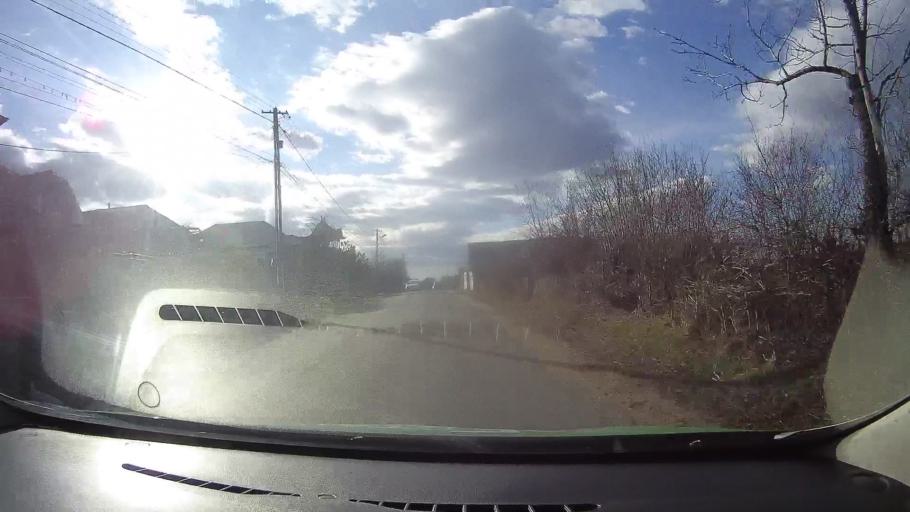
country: RO
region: Dambovita
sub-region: Comuna Ulmi
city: Ulmi
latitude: 44.8892
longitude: 25.5075
